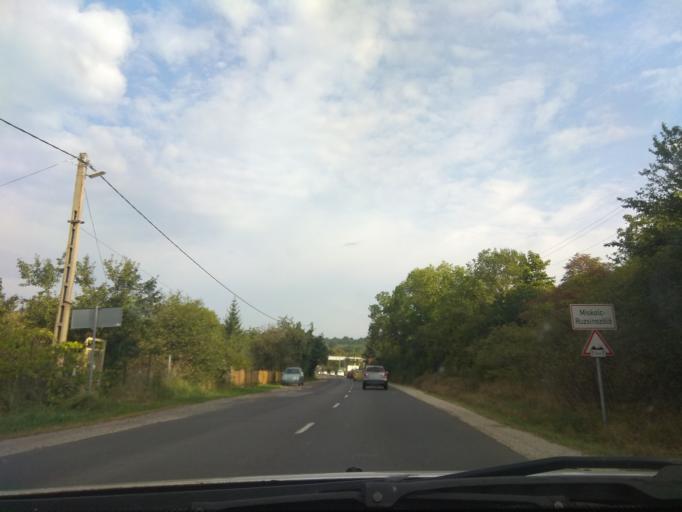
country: HU
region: Borsod-Abauj-Zemplen
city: Miskolc
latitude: 48.0847
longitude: 20.7695
